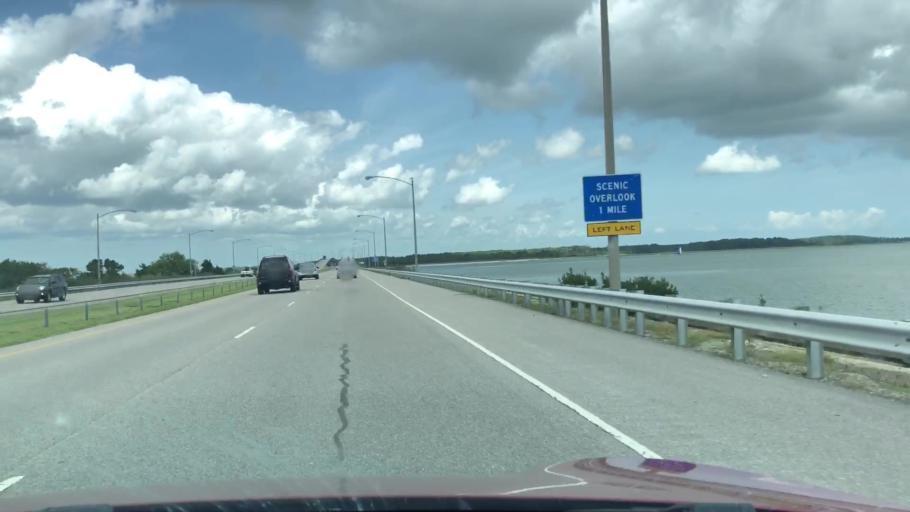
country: US
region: Virginia
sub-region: Northampton County
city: Cape Charles
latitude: 37.1062
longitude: -75.9691
